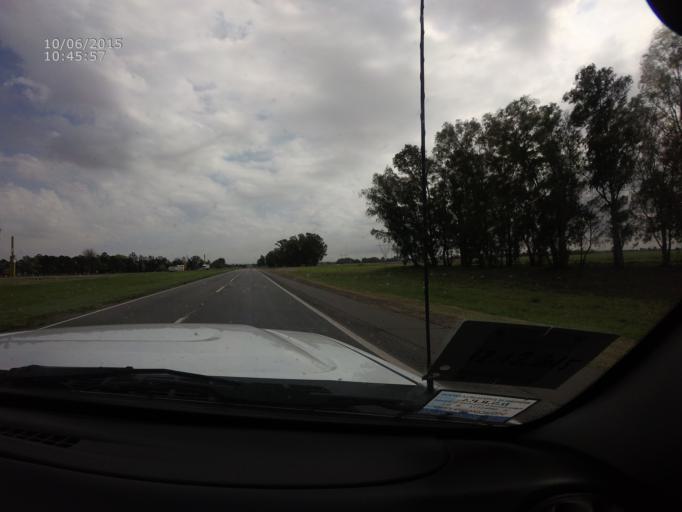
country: AR
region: Buenos Aires
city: San Nicolas de los Arroyos
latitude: -33.4246
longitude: -60.1777
